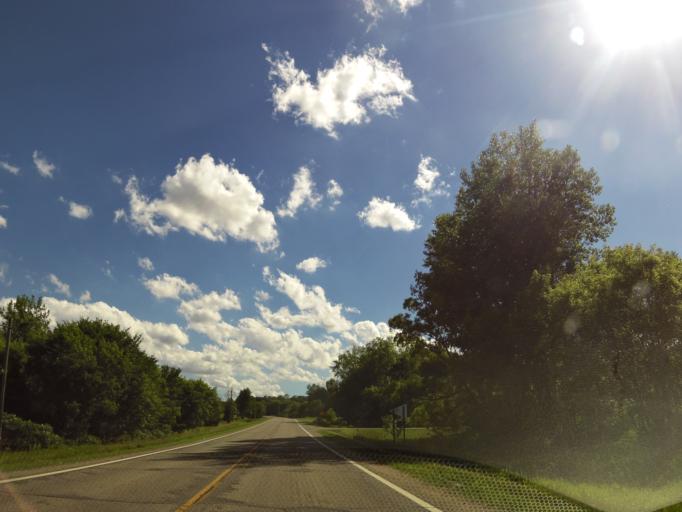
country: US
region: Minnesota
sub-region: Meeker County
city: Dassel
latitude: 45.1046
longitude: -94.3042
